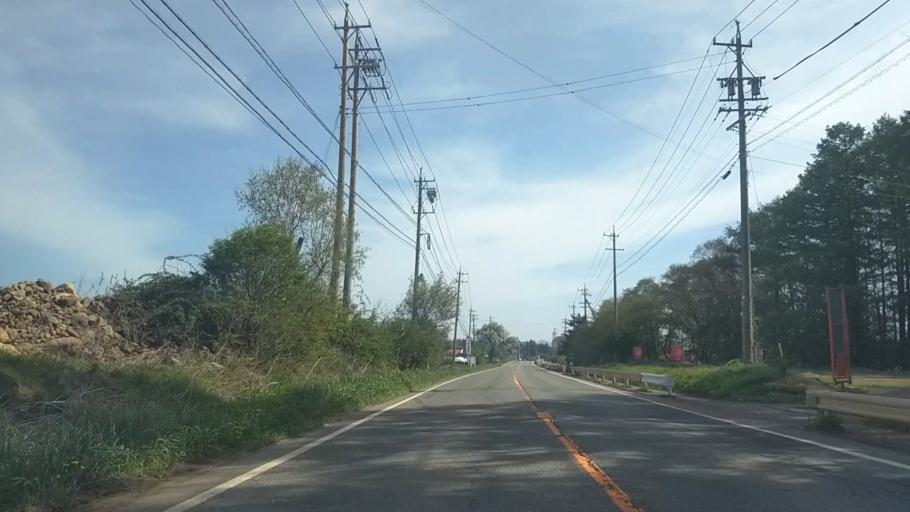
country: JP
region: Nagano
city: Saku
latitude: 35.9666
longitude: 138.4771
